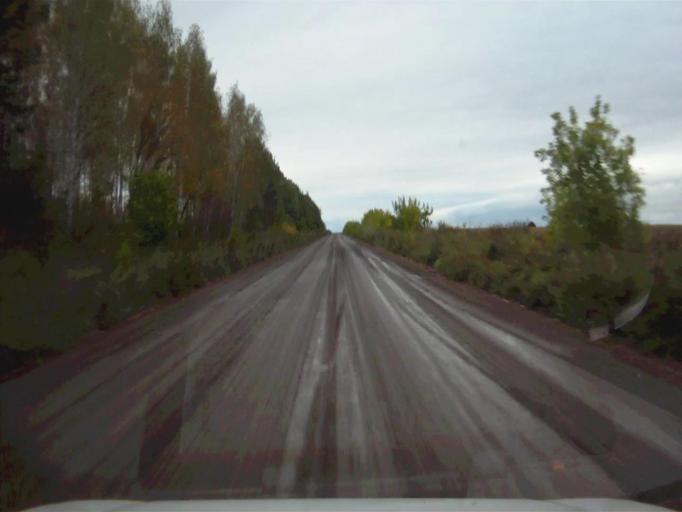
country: RU
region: Sverdlovsk
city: Mikhaylovsk
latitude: 56.1534
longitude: 59.2640
